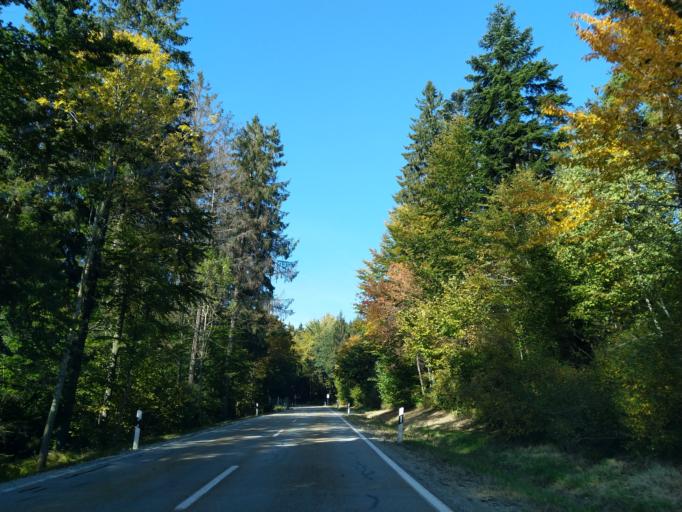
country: DE
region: Bavaria
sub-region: Lower Bavaria
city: Achslach
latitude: 48.9355
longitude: 12.9259
